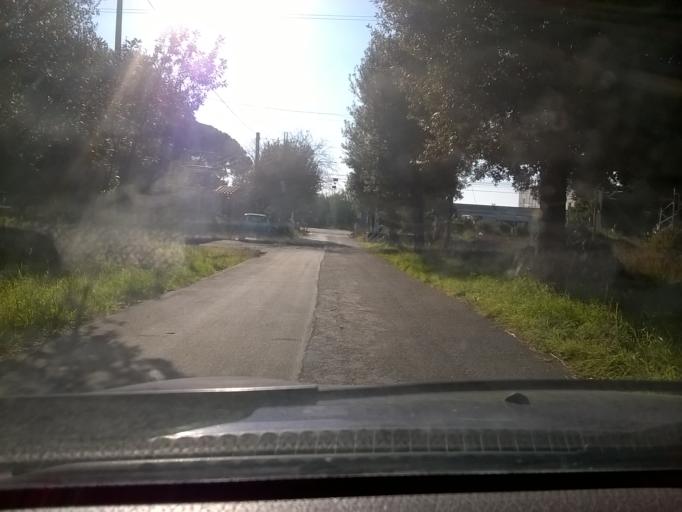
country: IT
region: Apulia
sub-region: Provincia di Taranto
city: Paolo VI
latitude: 40.5150
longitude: 17.2836
